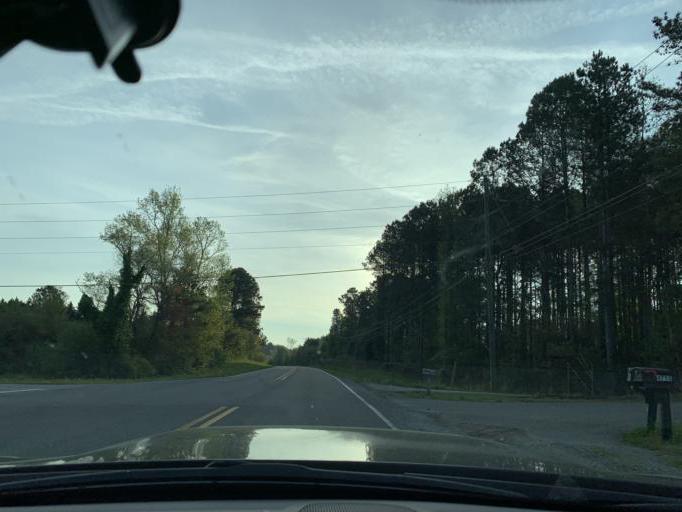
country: US
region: Georgia
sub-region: Forsyth County
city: Cumming
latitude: 34.2490
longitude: -84.1572
